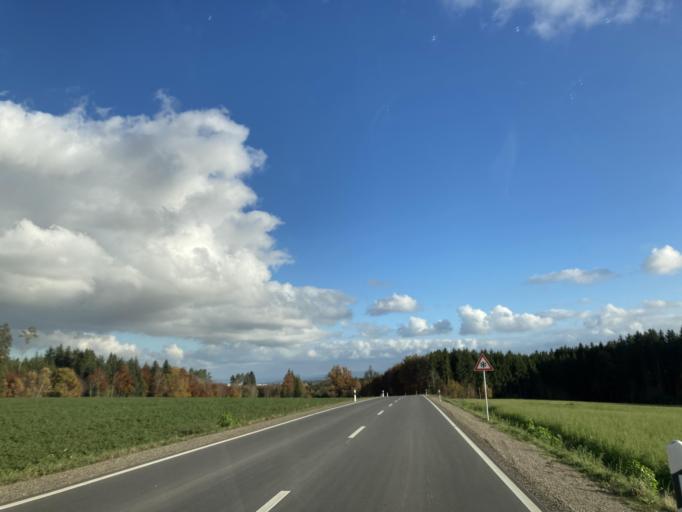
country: DE
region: Baden-Wuerttemberg
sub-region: Freiburg Region
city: Muhlheim am Bach
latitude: 48.4026
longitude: 8.6799
